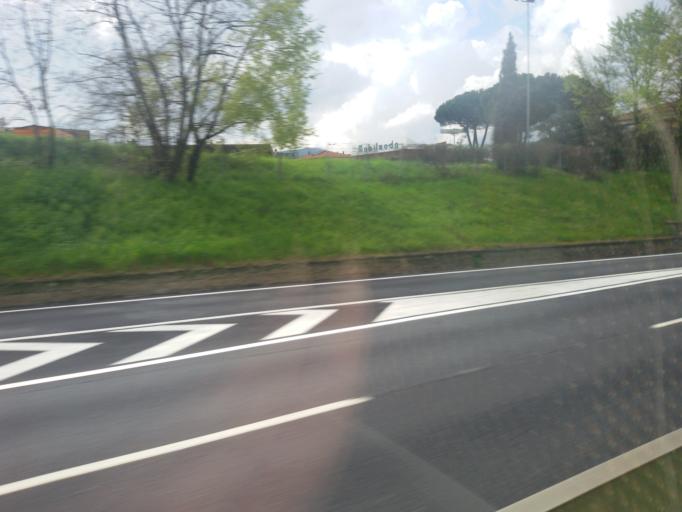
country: IT
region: Tuscany
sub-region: Province of Florence
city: Incisa in Val d'Arno
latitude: 43.6648
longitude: 11.4594
